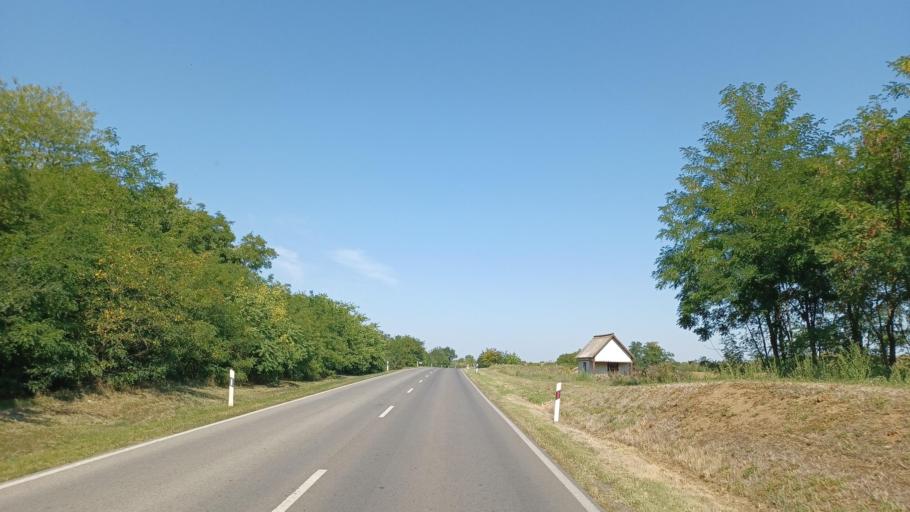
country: HU
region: Tolna
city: Nagydorog
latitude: 46.6380
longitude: 18.6518
